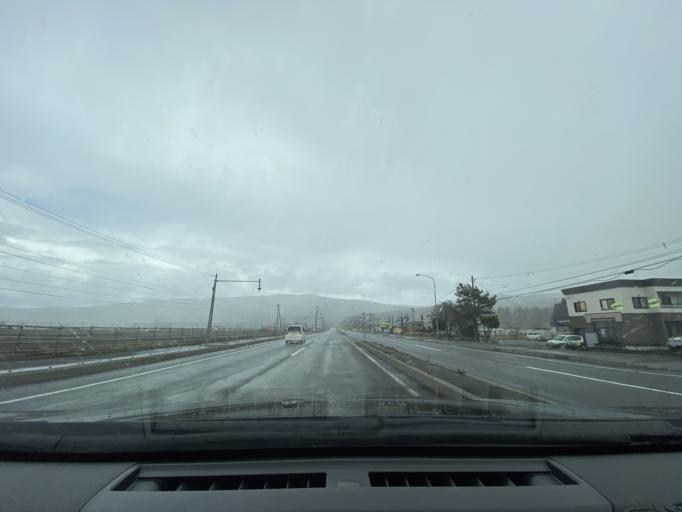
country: JP
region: Hokkaido
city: Fukagawa
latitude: 43.7214
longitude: 142.1834
